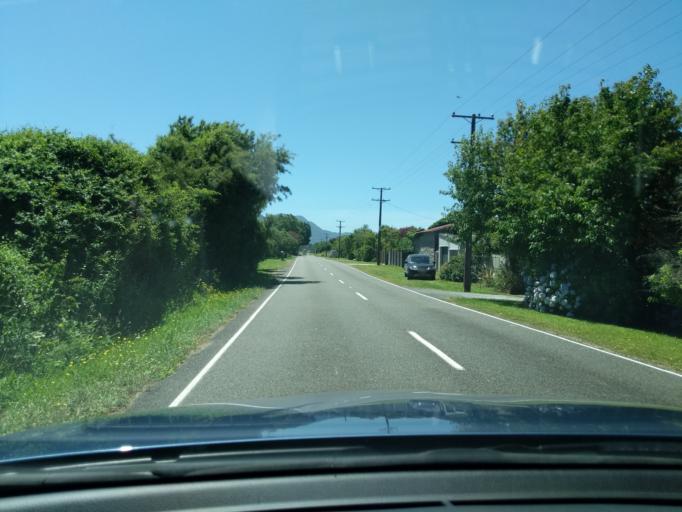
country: NZ
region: Tasman
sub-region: Tasman District
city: Takaka
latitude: -40.7249
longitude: 172.6378
